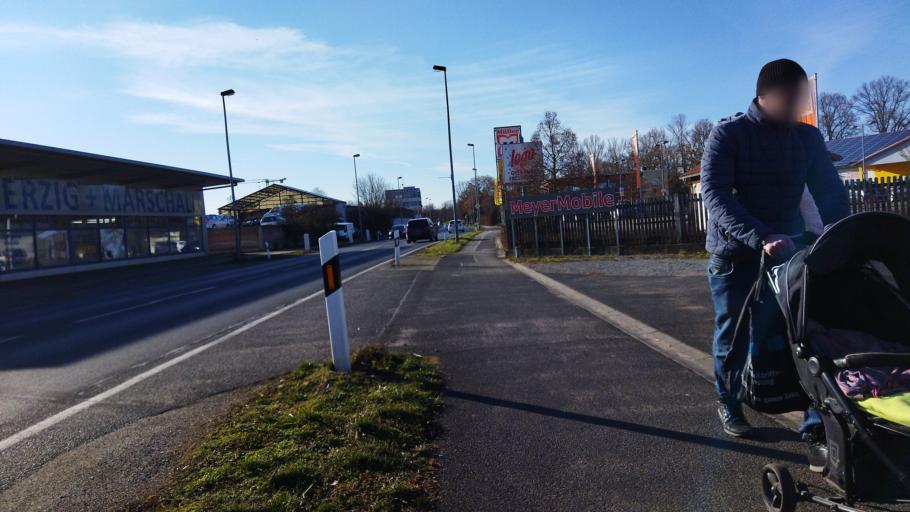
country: DE
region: Bavaria
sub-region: Regierungsbezirk Unterfranken
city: Sennfeld
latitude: 50.0383
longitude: 10.2470
